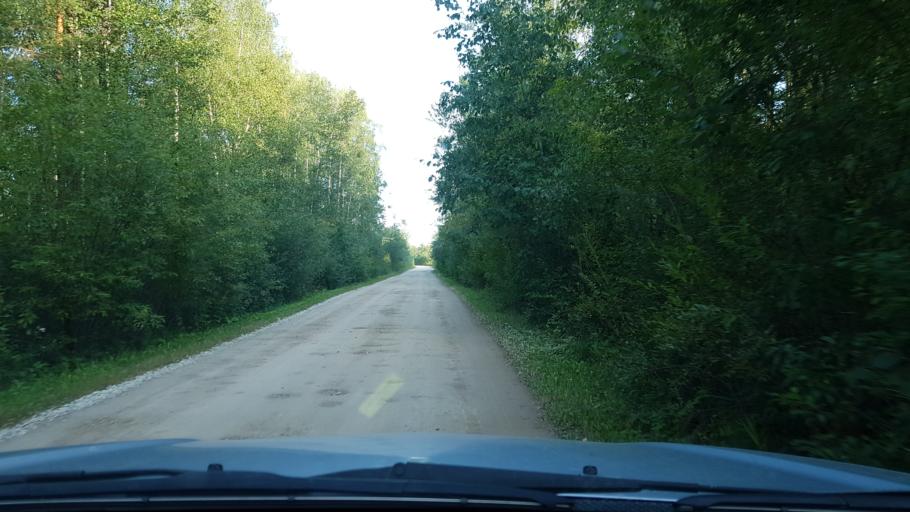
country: EE
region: Ida-Virumaa
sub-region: Sillamaee linn
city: Sillamae
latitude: 59.2616
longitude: 27.9218
